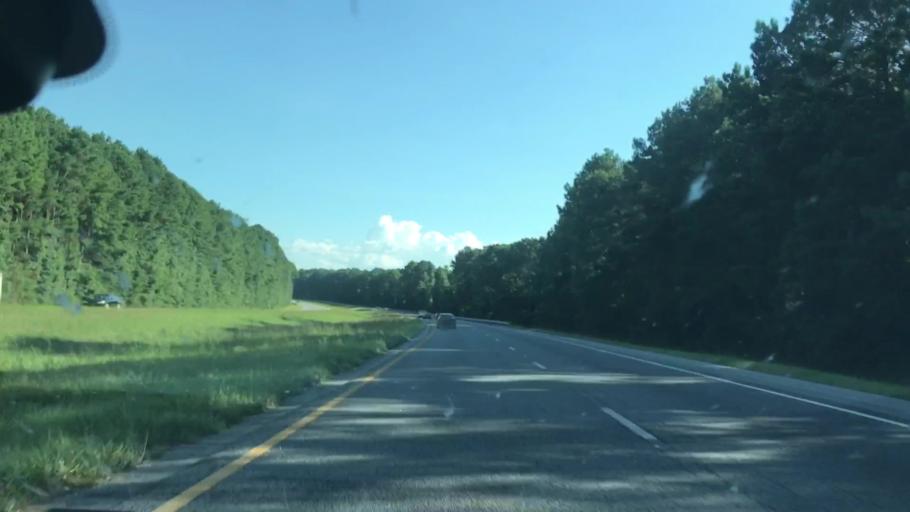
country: US
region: Georgia
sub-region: Harris County
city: Hamilton
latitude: 32.7759
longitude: -85.0210
